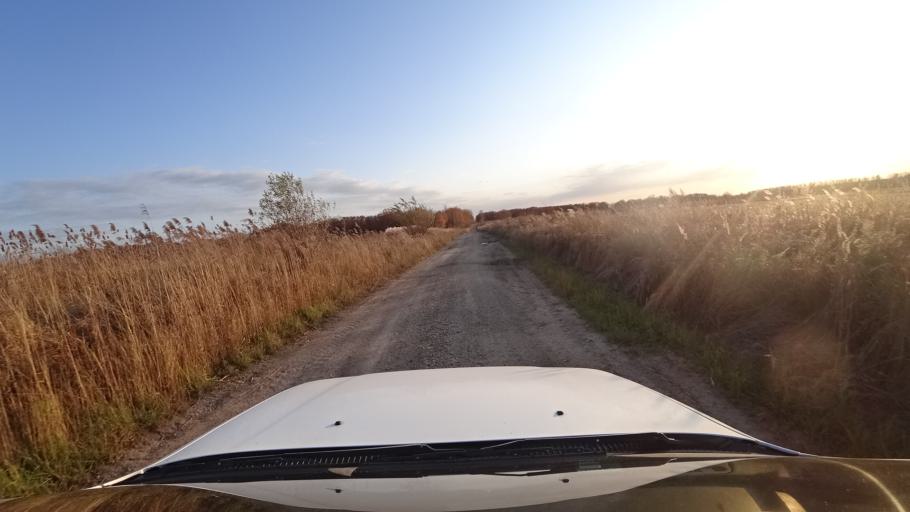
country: RU
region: Primorskiy
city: Lazo
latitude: 45.8089
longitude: 133.6070
